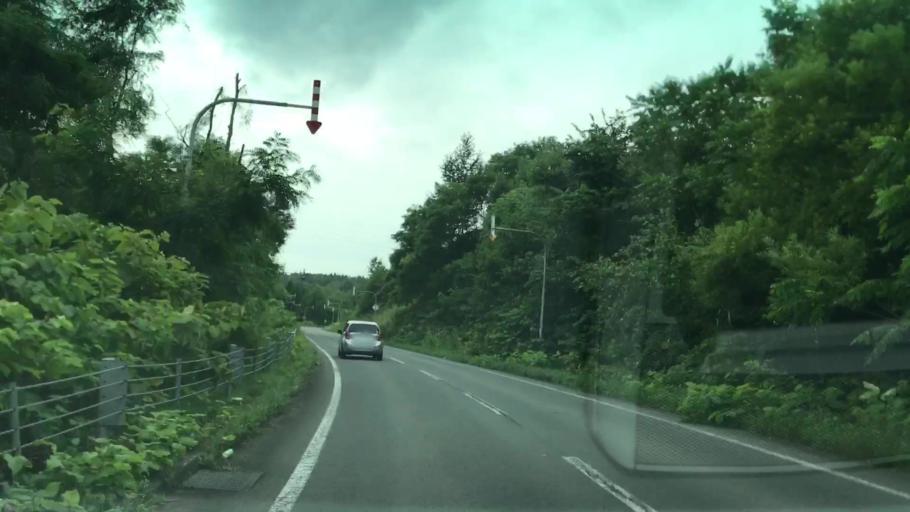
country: JP
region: Hokkaido
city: Yoichi
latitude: 43.1423
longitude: 140.8205
